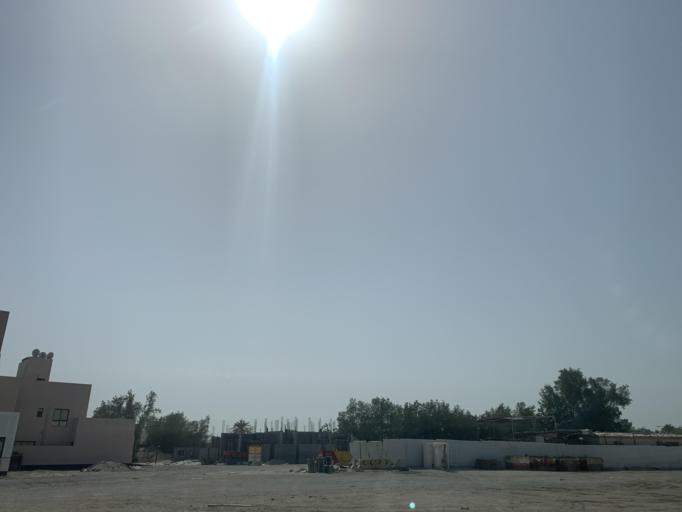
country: BH
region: Manama
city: Jidd Hafs
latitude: 26.2112
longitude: 50.5132
